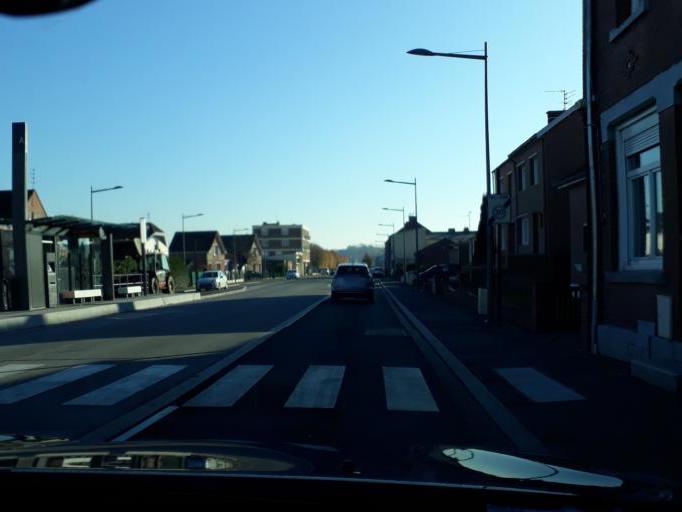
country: FR
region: Nord-Pas-de-Calais
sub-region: Departement du Nord
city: Guesnain
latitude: 50.3455
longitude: 3.1505
